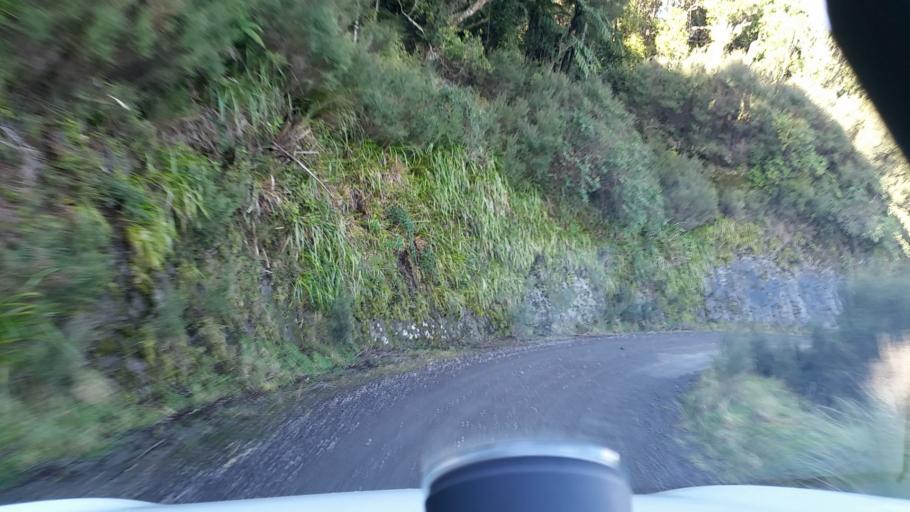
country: NZ
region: Taranaki
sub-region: South Taranaki District
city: Eltham
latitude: -39.4035
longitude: 174.5614
